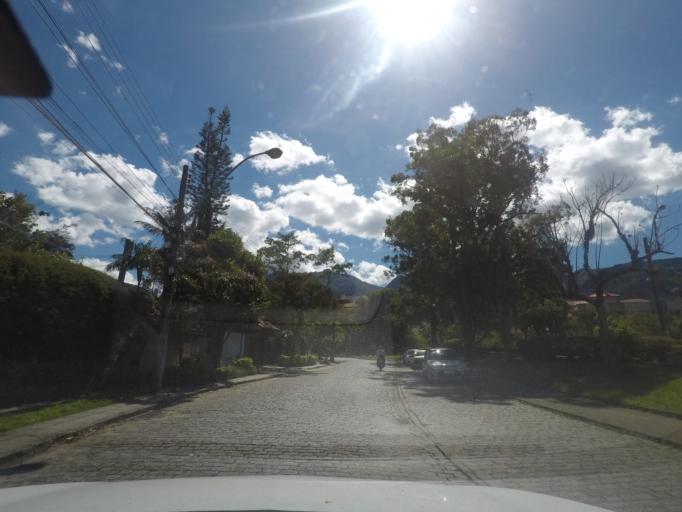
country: BR
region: Rio de Janeiro
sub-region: Teresopolis
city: Teresopolis
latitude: -22.4349
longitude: -42.9740
